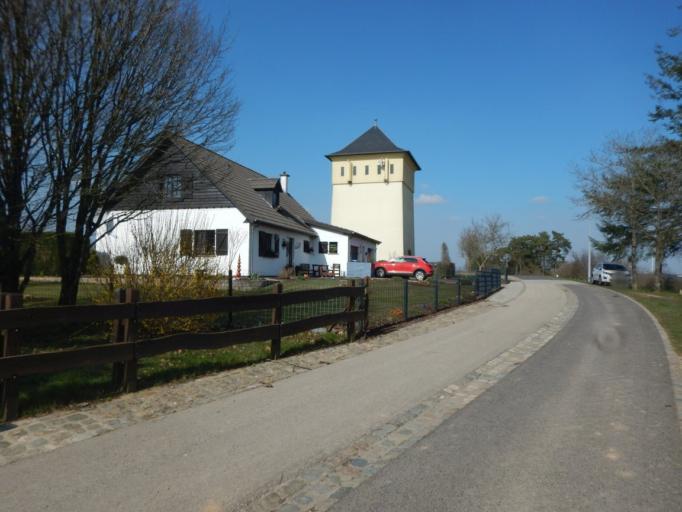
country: LU
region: Diekirch
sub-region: Canton de Diekirch
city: Bourscheid
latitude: 49.9510
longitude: 6.0811
